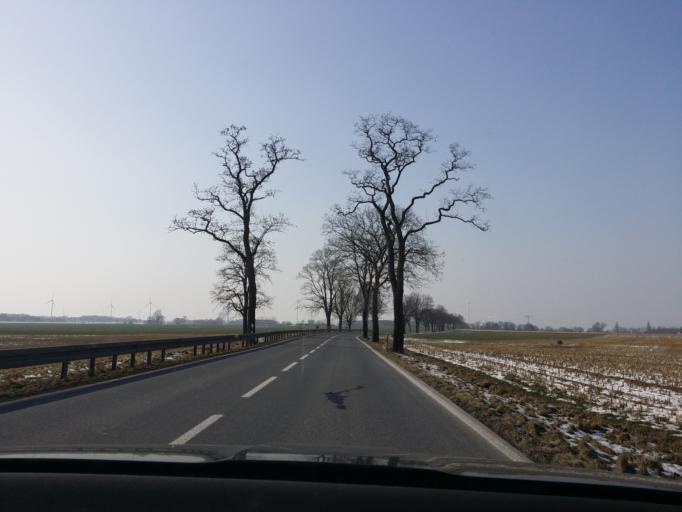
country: DE
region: Brandenburg
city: Pritzwalk
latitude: 53.1375
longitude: 12.2612
